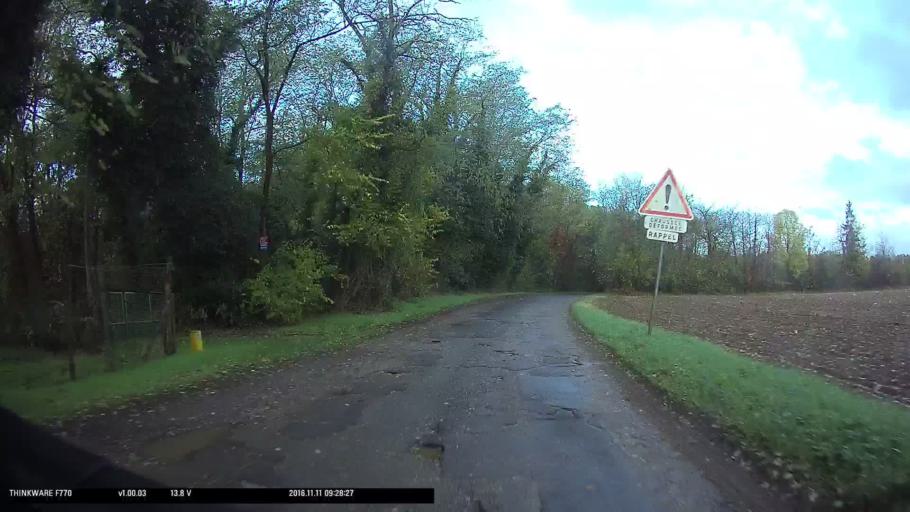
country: FR
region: Ile-de-France
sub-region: Departement du Val-d'Oise
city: Osny
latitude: 49.0706
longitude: 2.0429
